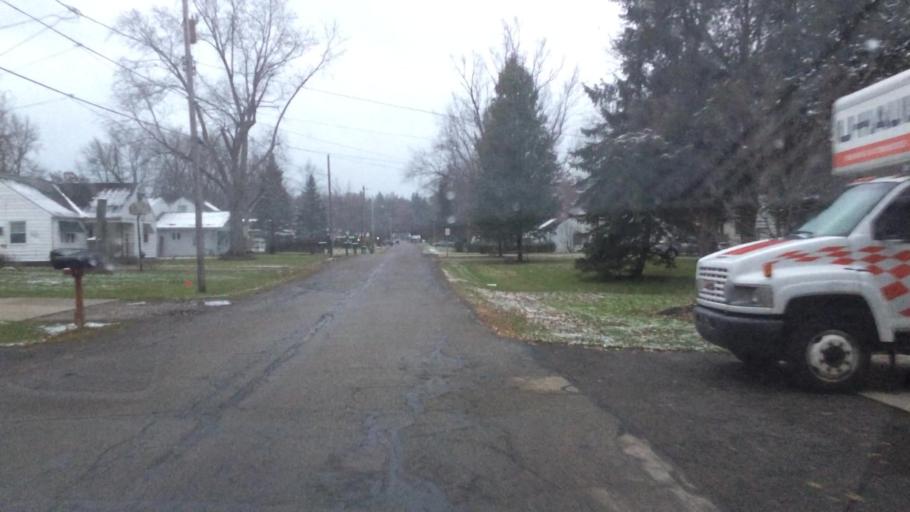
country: US
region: Ohio
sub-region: Cuyahoga County
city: Olmsted Falls
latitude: 41.3499
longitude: -81.8912
